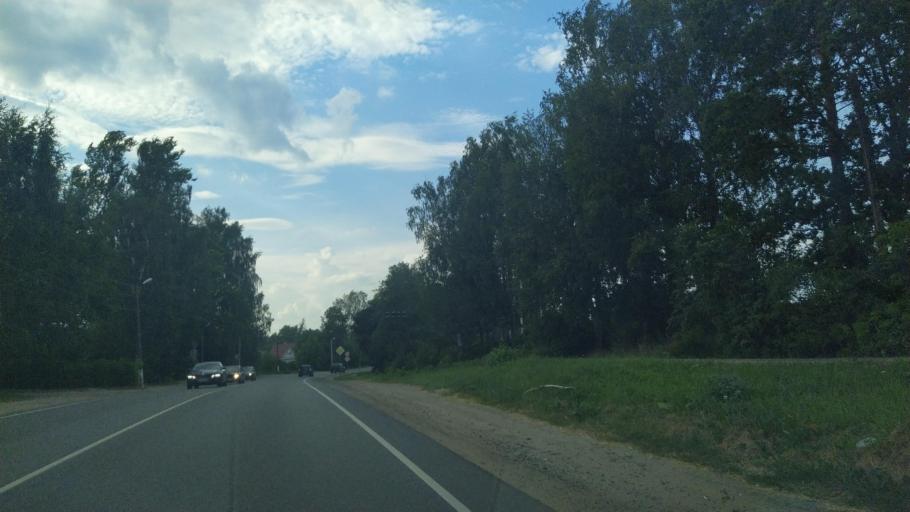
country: RU
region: Leningrad
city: Toksovo
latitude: 60.1459
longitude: 30.5248
